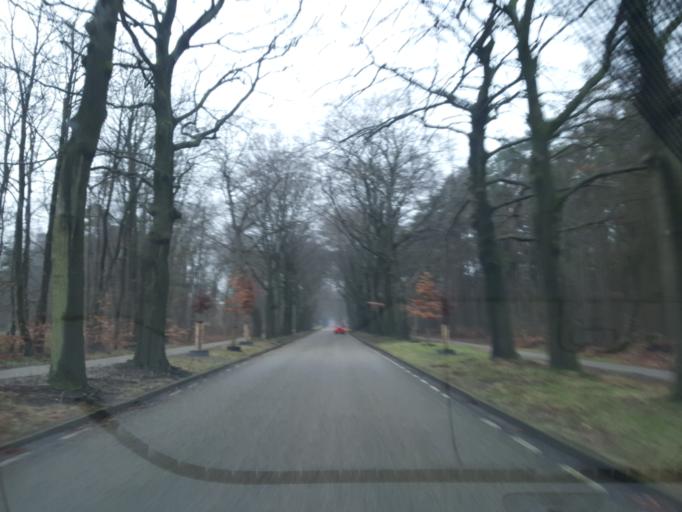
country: NL
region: North Holland
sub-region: Gemeente Bussum
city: Bussum
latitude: 52.2512
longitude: 5.1618
